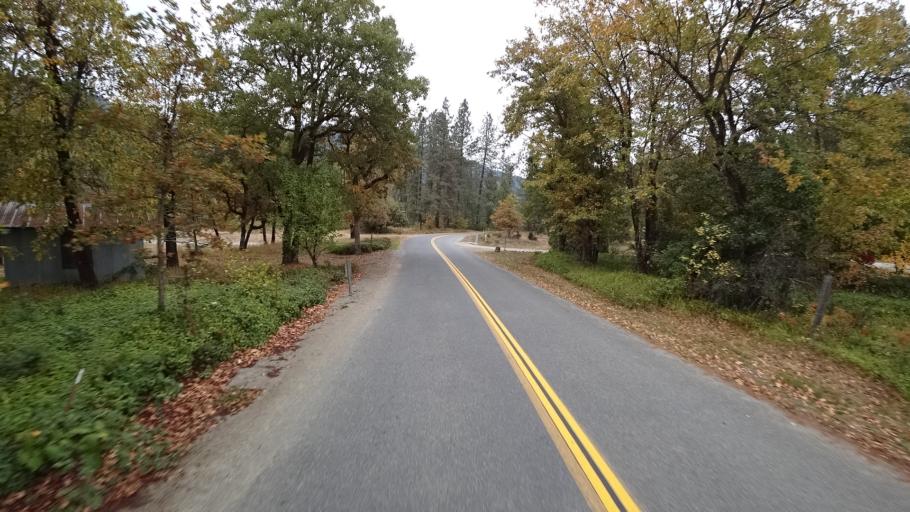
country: US
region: California
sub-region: Siskiyou County
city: Happy Camp
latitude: 41.7811
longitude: -123.3927
